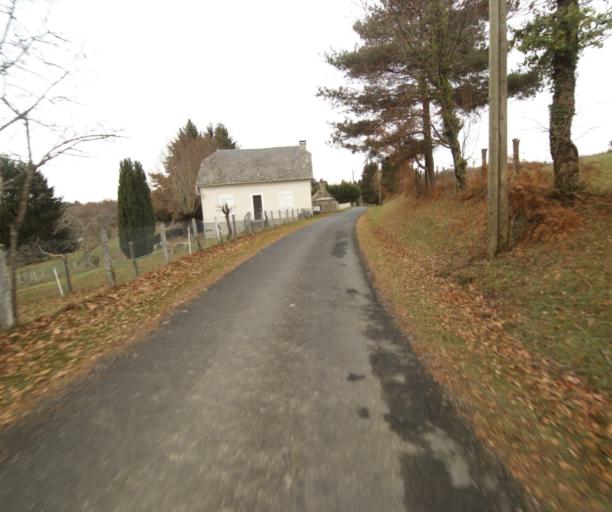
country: FR
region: Limousin
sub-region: Departement de la Correze
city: Saint-Mexant
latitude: 45.2543
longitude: 1.6558
